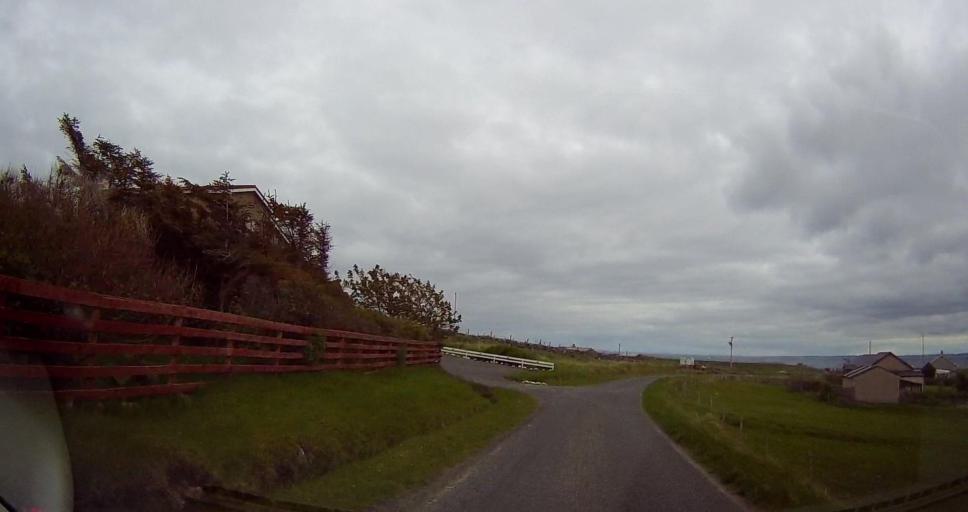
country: GB
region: Scotland
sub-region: Shetland Islands
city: Shetland
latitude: 60.5023
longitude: -1.0575
